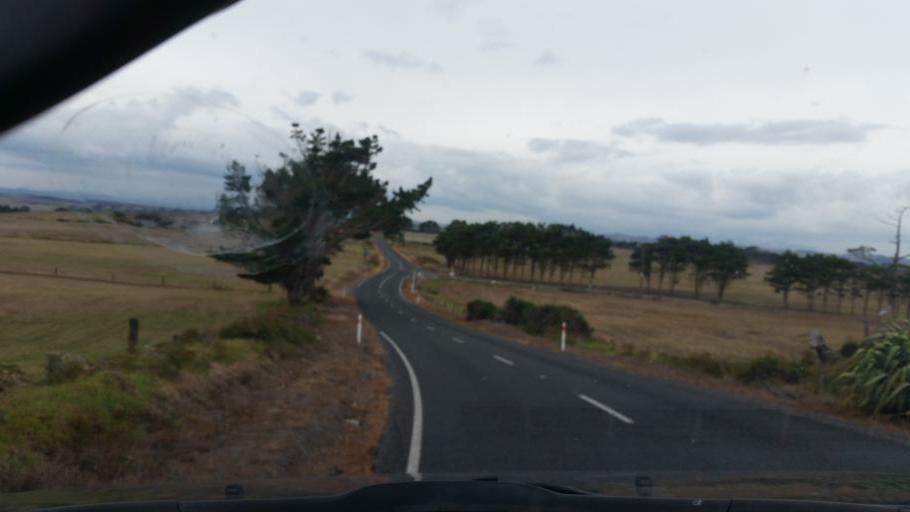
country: NZ
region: Northland
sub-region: Kaipara District
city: Dargaville
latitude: -36.0585
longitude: 173.8716
